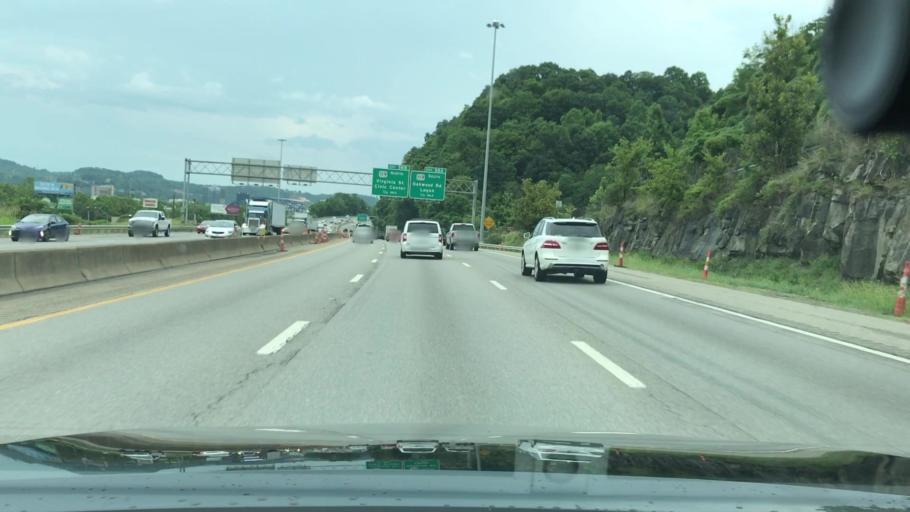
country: US
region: West Virginia
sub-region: Kanawha County
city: Charleston
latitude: 38.3585
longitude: -81.6616
